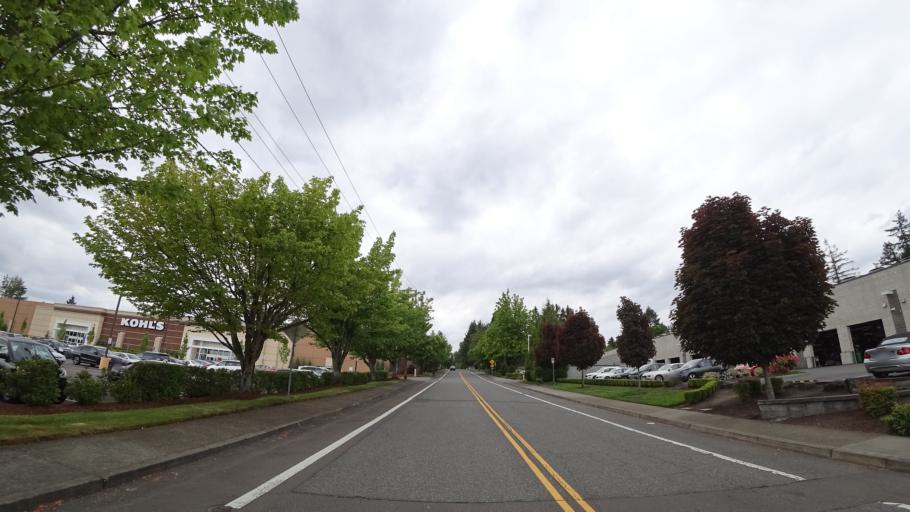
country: US
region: Oregon
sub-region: Washington County
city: Beaverton
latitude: 45.4923
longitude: -122.7895
